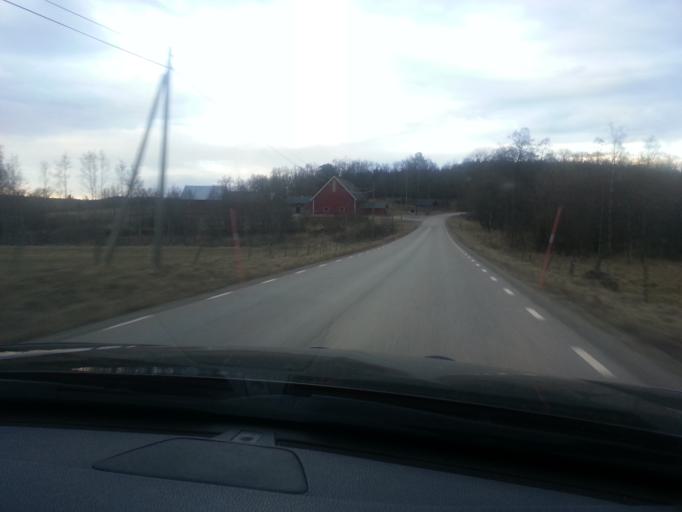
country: SE
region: Joenkoeping
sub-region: Vetlanda Kommun
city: Vetlanda
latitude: 57.3162
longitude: 15.1269
